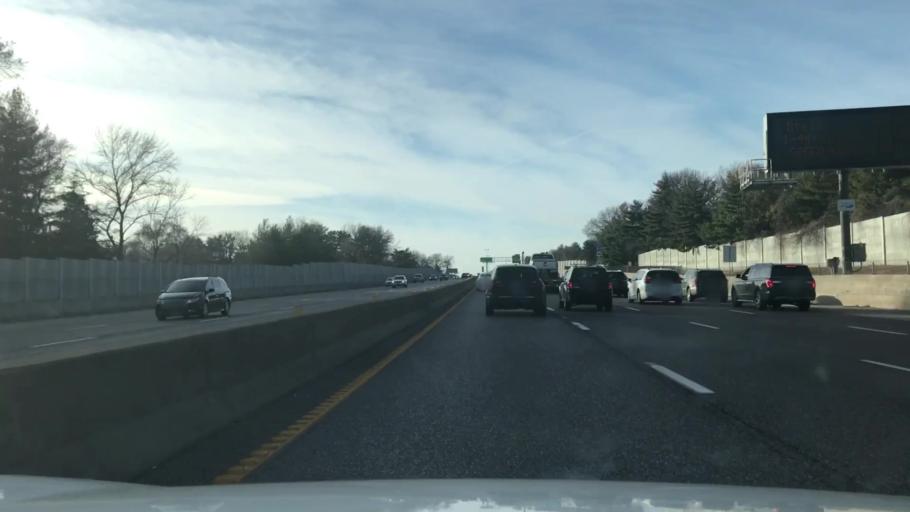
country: US
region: Missouri
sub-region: Saint Louis County
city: Frontenac
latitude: 38.6361
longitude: -90.4224
